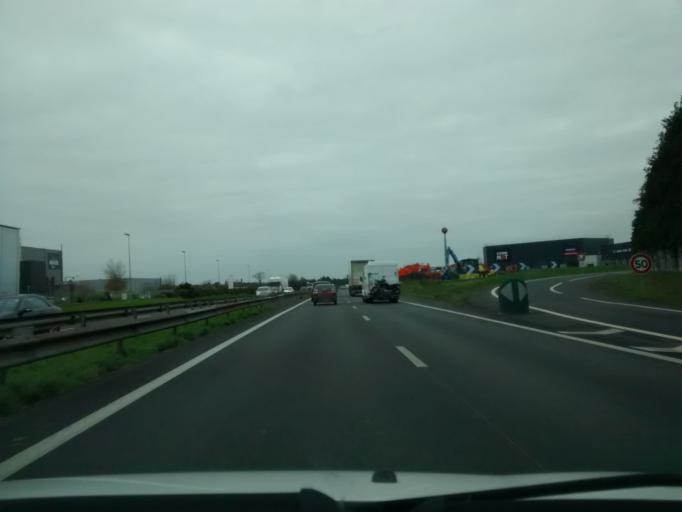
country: FR
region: Brittany
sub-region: Departement d'Ille-et-Vilaine
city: Servon-sur-Vilaine
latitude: 48.1028
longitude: -1.4563
